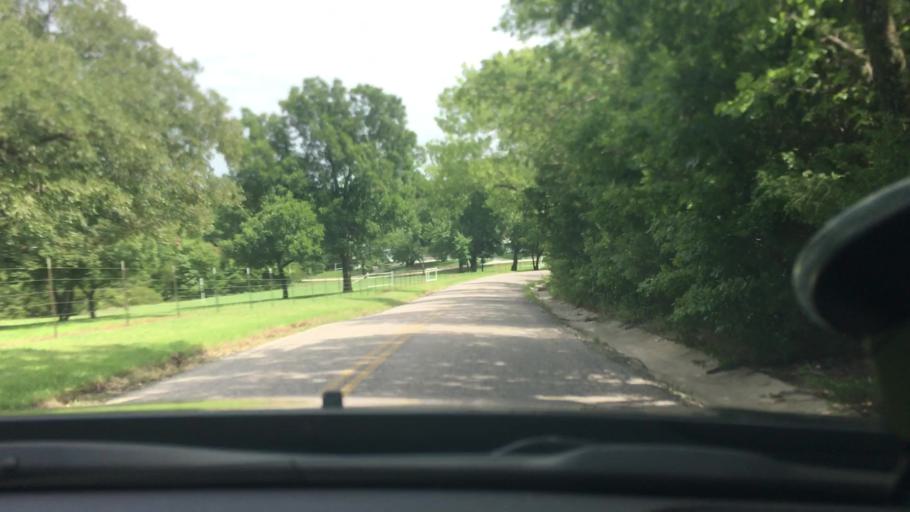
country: US
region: Oklahoma
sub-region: Pontotoc County
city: Ada
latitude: 34.8128
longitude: -96.7106
